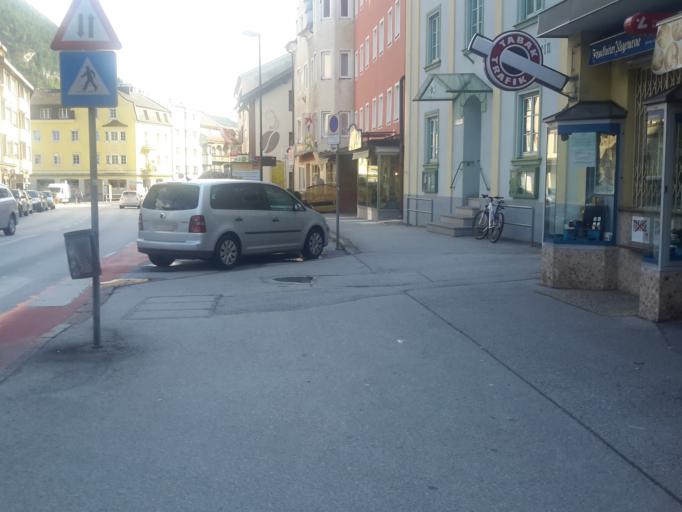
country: AT
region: Tyrol
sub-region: Politischer Bezirk Kufstein
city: Kufstein
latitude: 47.5809
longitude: 12.1703
